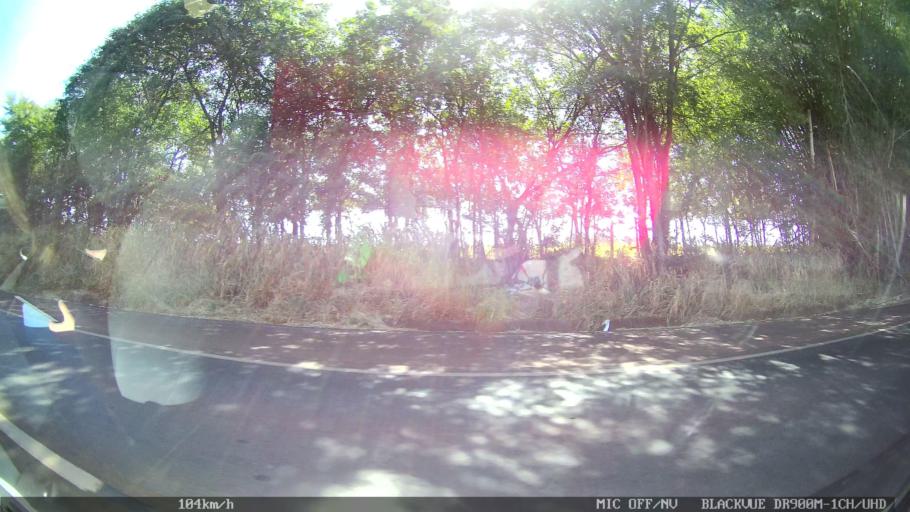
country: BR
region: Sao Paulo
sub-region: Barretos
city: Barretos
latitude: -20.5331
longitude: -48.6012
